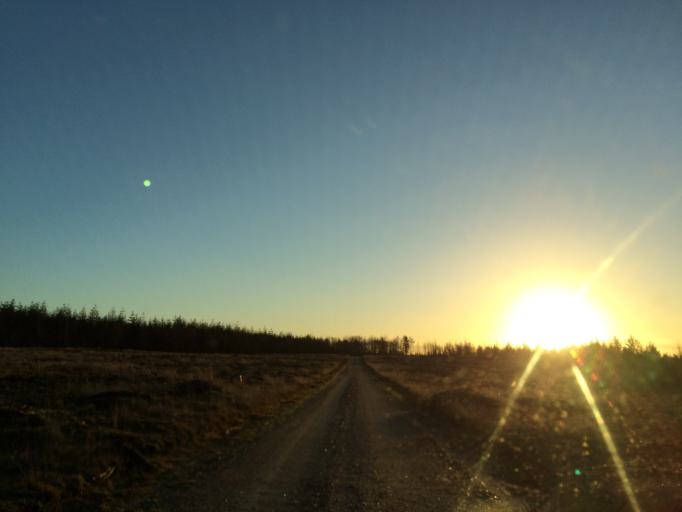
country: DK
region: Central Jutland
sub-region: Ringkobing-Skjern Kommune
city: Videbaek
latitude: 56.2188
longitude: 8.5168
